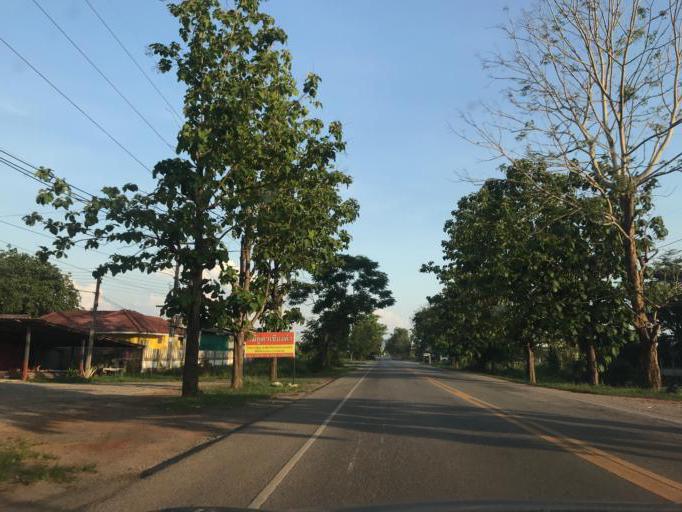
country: TH
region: Phayao
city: Chiang Kham
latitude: 19.5300
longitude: 100.2931
